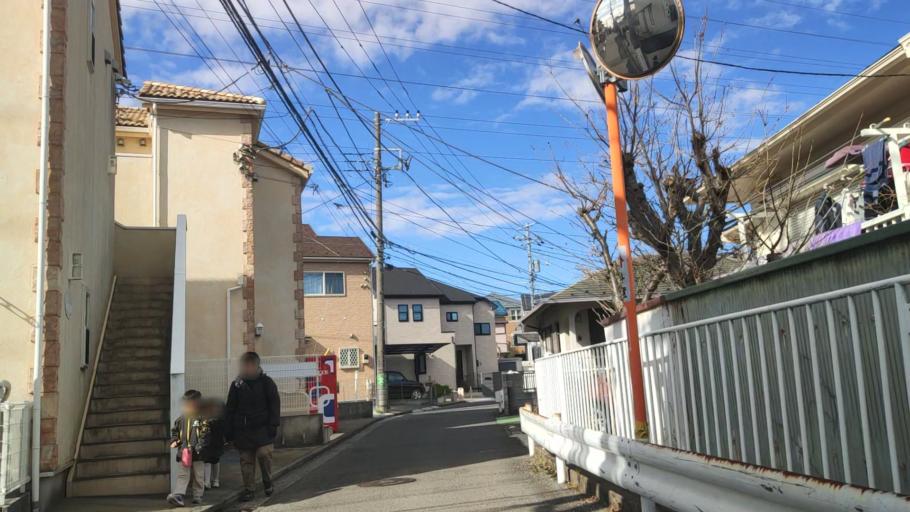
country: JP
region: Kanagawa
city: Yokohama
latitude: 35.4699
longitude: 139.5836
